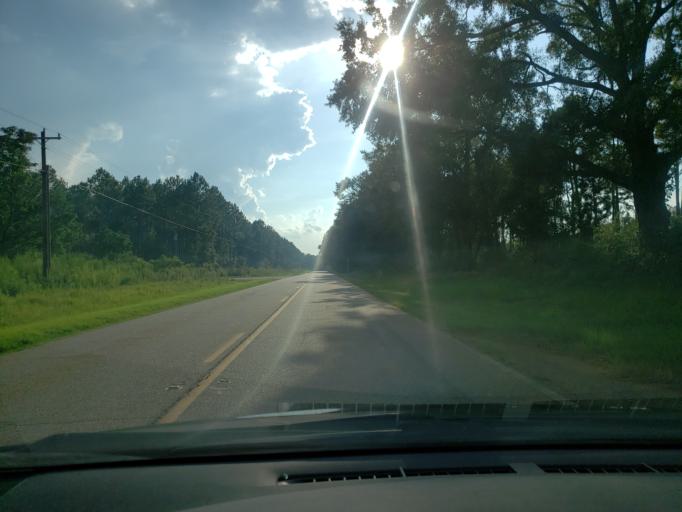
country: US
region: Georgia
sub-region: Dougherty County
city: Albany
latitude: 31.5732
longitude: -84.3241
